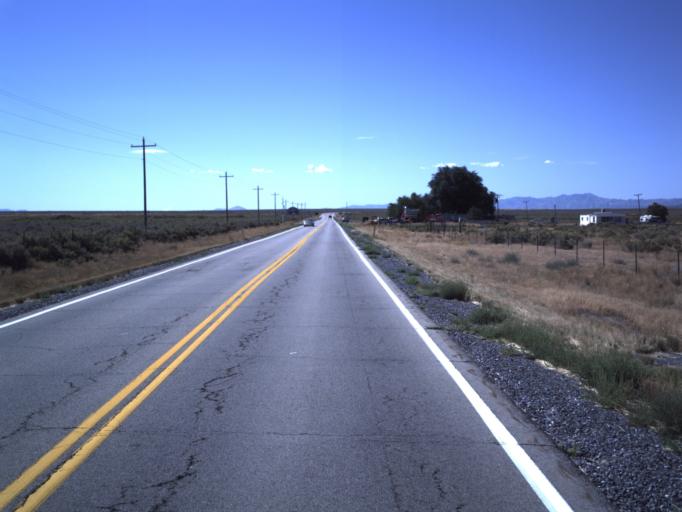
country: US
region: Utah
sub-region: Tooele County
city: Tooele
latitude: 40.3916
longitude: -112.3862
